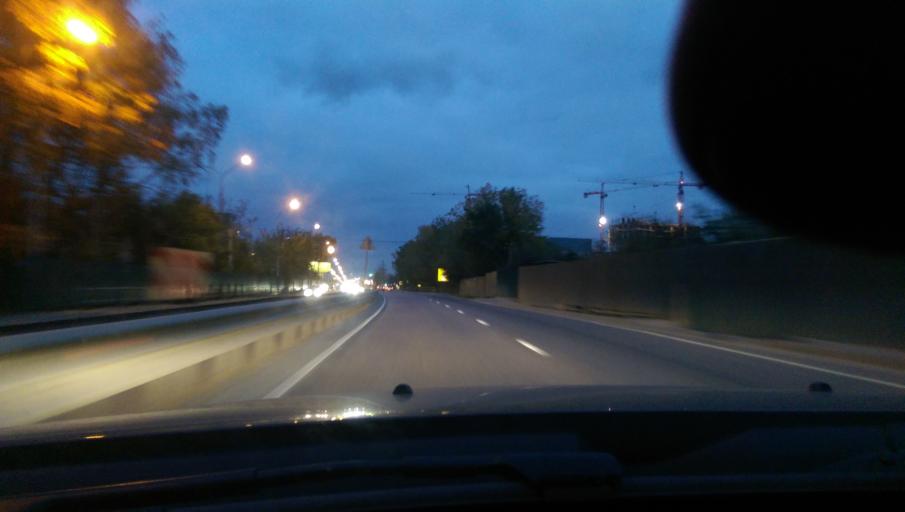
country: RU
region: Moscow
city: Vatutino
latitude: 55.9245
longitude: 37.6620
